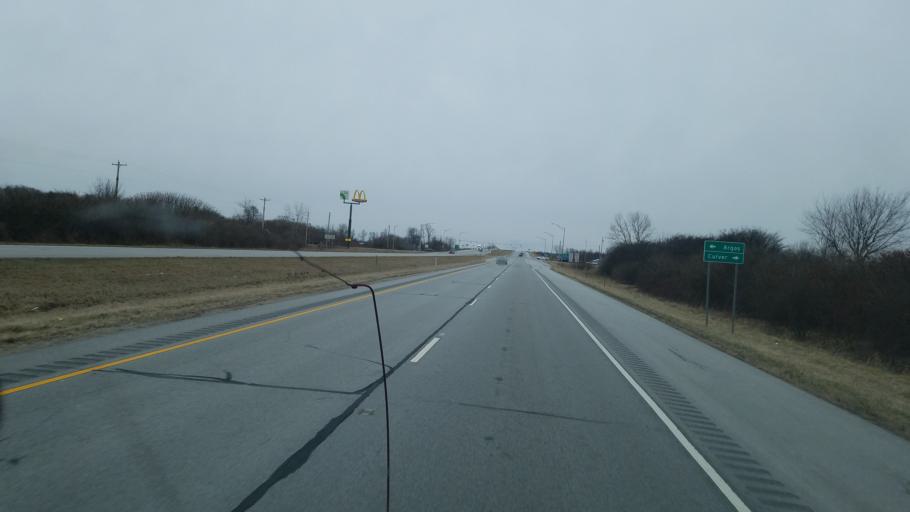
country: US
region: Indiana
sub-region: Marshall County
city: Argos
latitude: 41.2410
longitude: -86.2616
